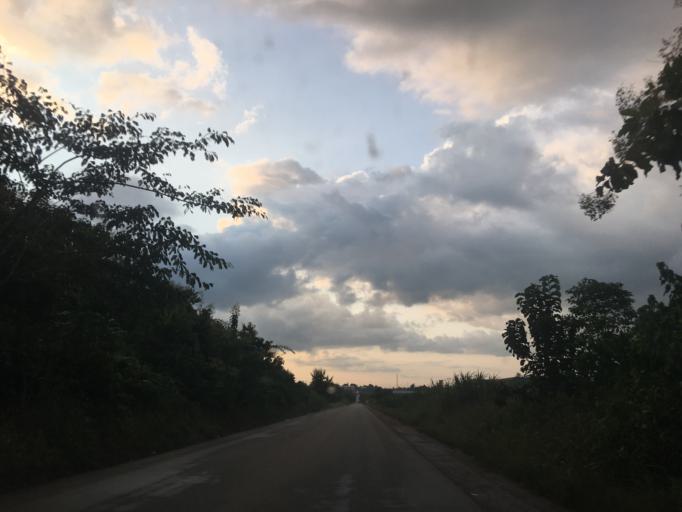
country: GH
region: Western
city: Bibiani
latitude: 6.7720
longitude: -2.5116
